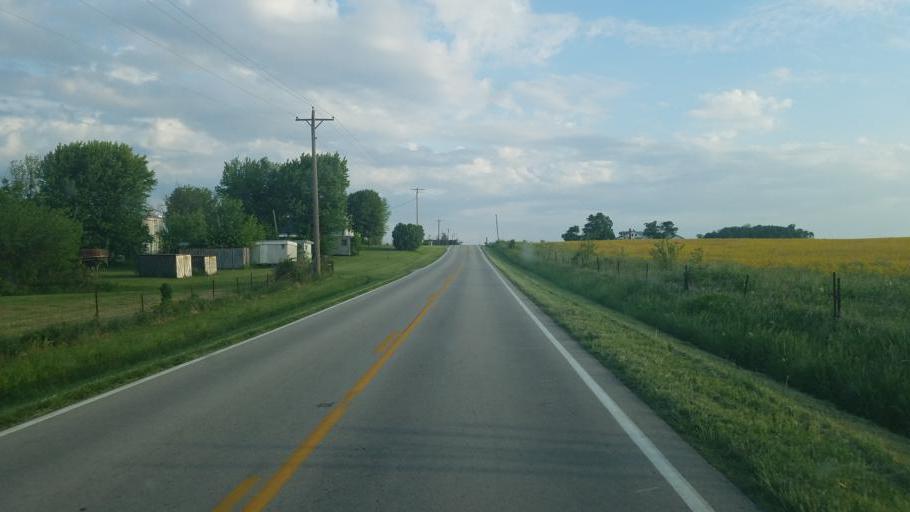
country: US
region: Ohio
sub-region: Highland County
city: Leesburg
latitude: 39.3934
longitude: -83.5966
